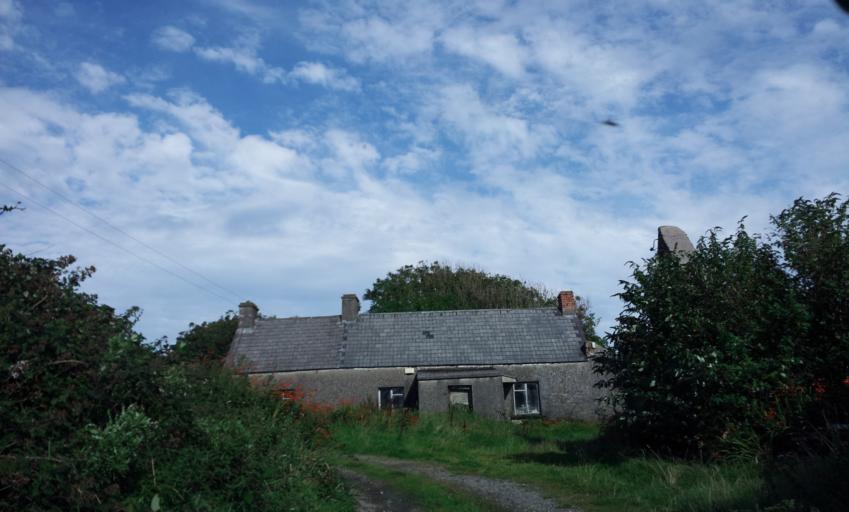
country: IE
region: Munster
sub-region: Ciarrai
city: Dingle
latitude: 52.1348
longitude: -10.3616
